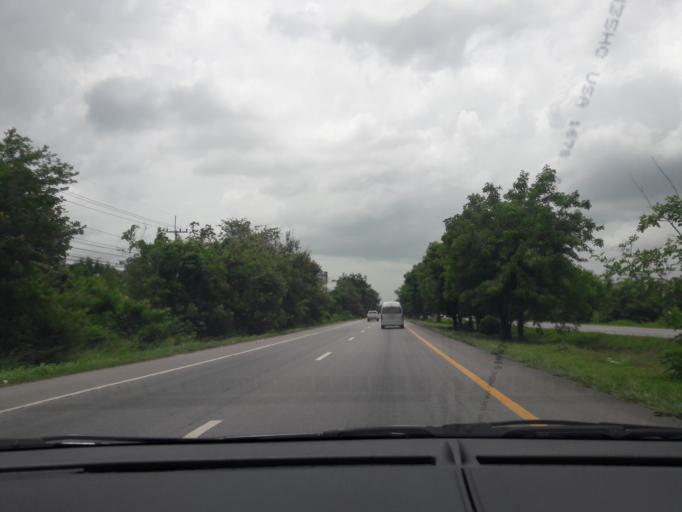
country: TH
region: Nakhon Ratchasima
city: Chaloem Phra Kiat
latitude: 15.0794
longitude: 102.2251
